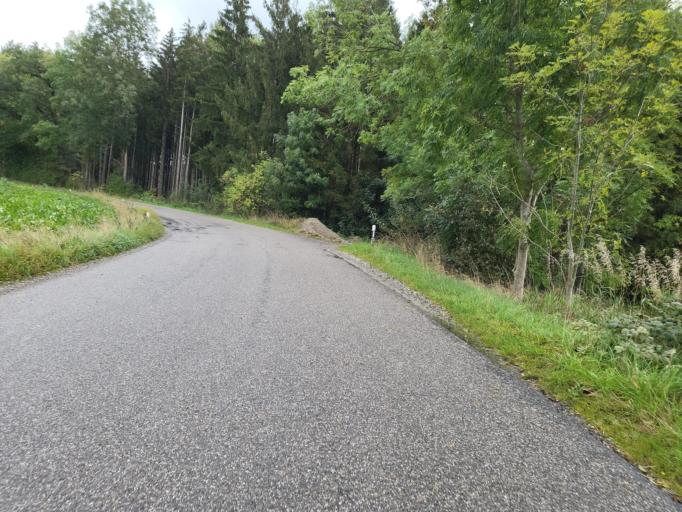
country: DE
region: Bavaria
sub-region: Upper Bavaria
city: Alling
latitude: 48.1561
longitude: 11.2849
